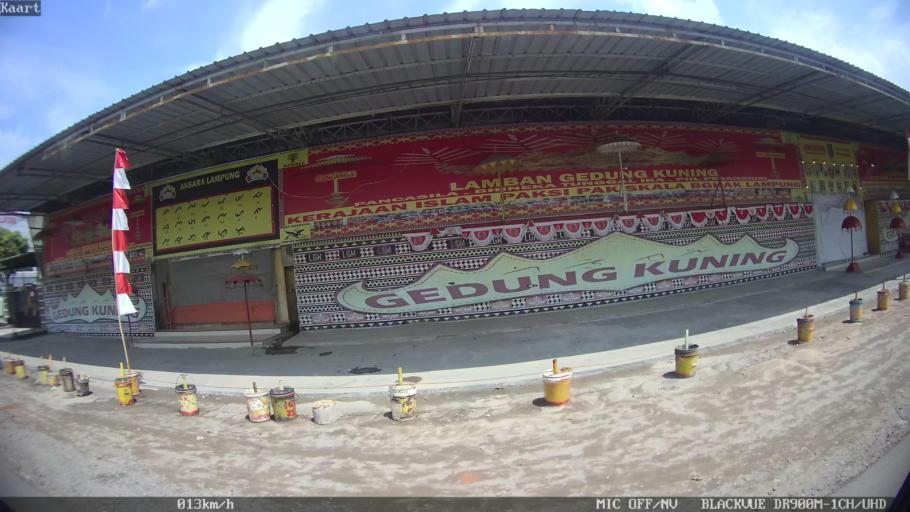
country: ID
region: Lampung
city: Kedaton
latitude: -5.3603
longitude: 105.3047
